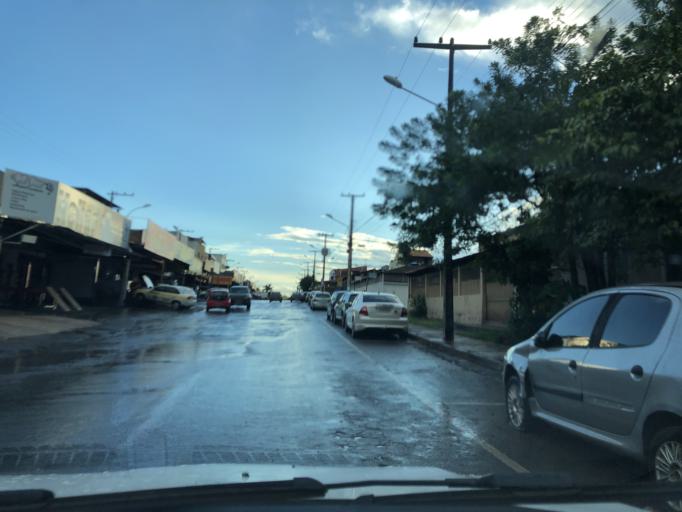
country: BR
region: Federal District
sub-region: Brasilia
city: Brasilia
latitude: -15.8699
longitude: -47.9625
